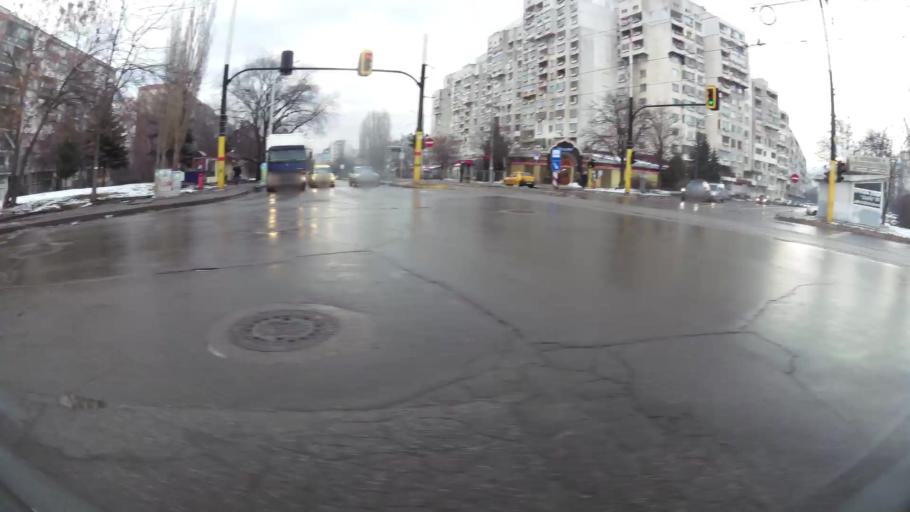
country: BG
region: Sofia-Capital
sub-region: Stolichna Obshtina
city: Sofia
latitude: 42.7023
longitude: 23.2856
